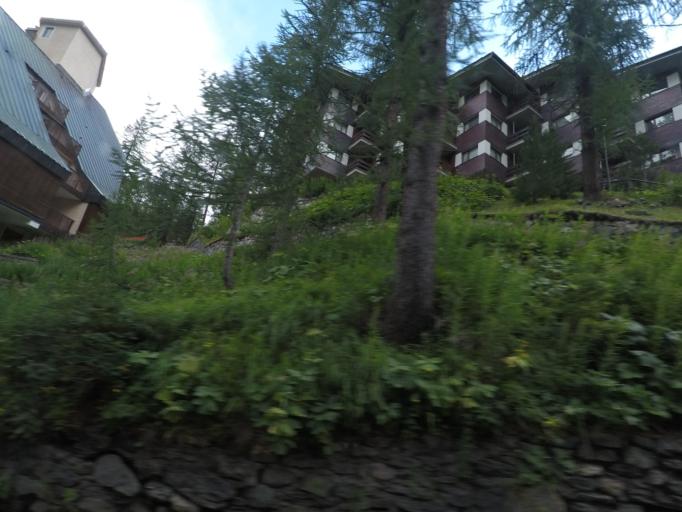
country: IT
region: Aosta Valley
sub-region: Valle d'Aosta
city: Paquier
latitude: 45.9322
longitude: 7.6309
